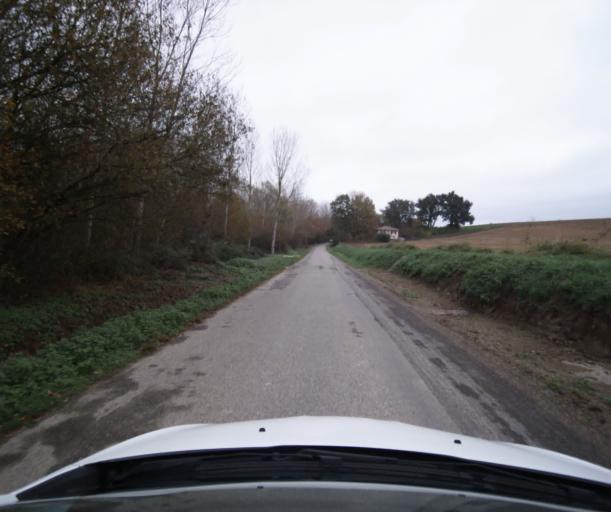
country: FR
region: Midi-Pyrenees
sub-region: Departement du Tarn-et-Garonne
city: Moissac
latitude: 44.0721
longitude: 1.1237
